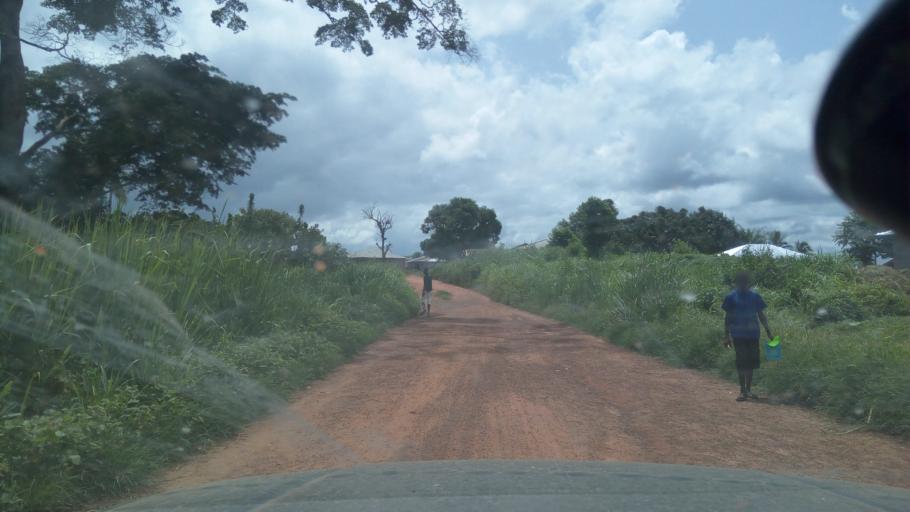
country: SL
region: Eastern Province
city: Kenema
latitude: 7.8788
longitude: -11.1580
